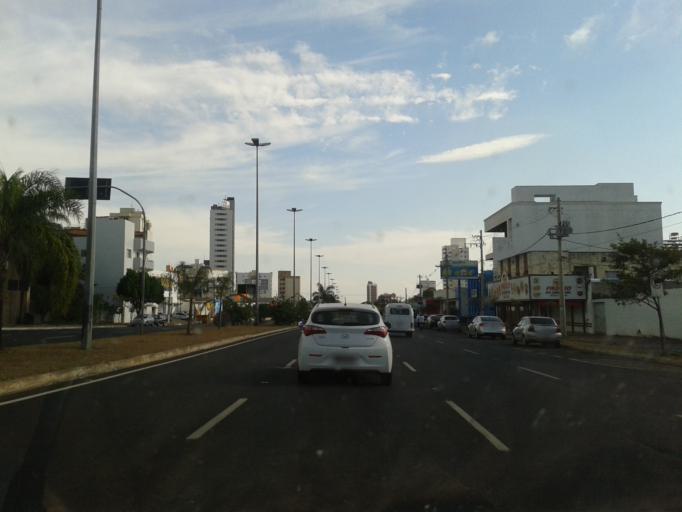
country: BR
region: Minas Gerais
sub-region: Uberlandia
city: Uberlandia
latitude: -18.9147
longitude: -48.2626
